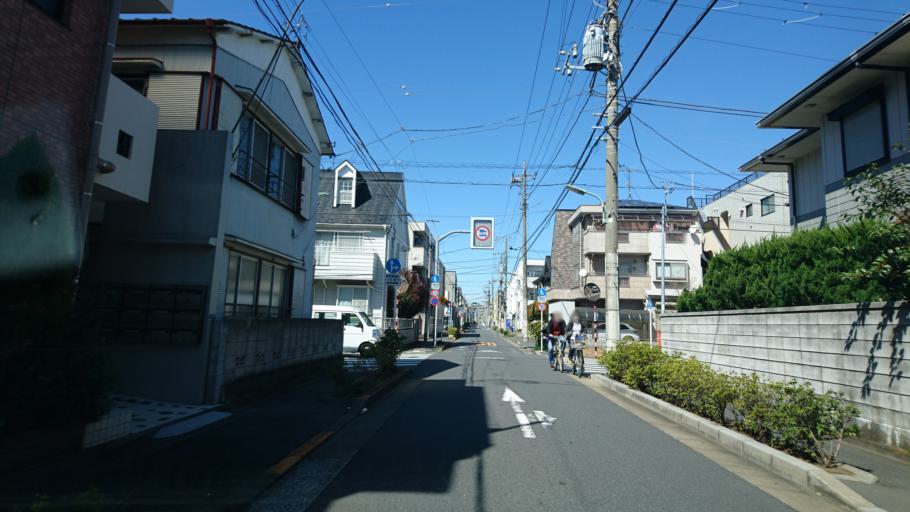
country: JP
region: Kanagawa
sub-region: Kawasaki-shi
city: Kawasaki
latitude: 35.5675
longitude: 139.7010
